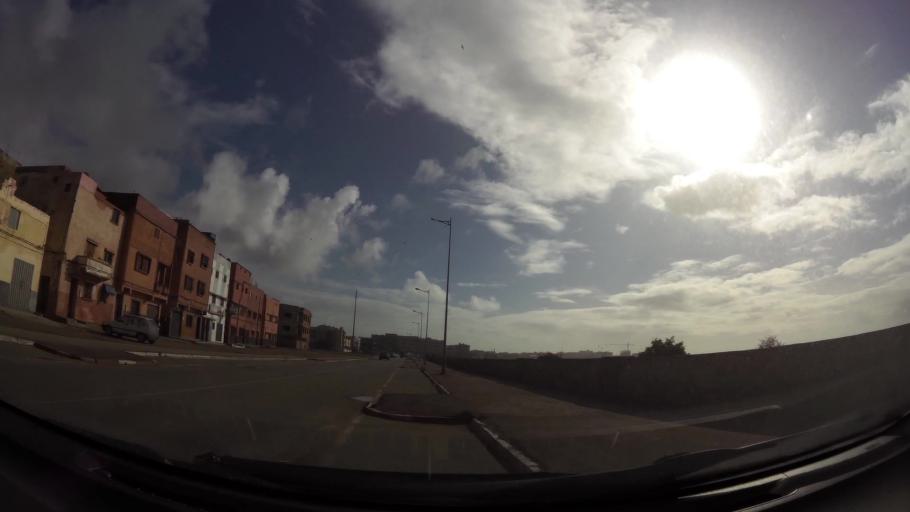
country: MA
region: Doukkala-Abda
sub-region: El-Jadida
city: El Jadida
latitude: 33.2575
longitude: -8.5173
